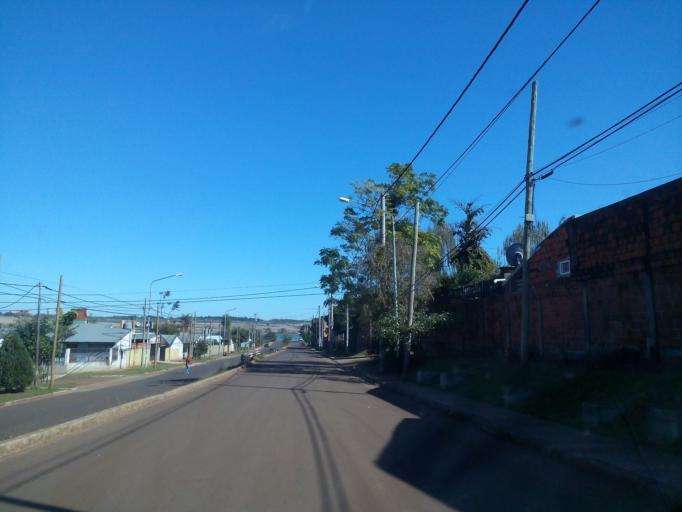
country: AR
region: Misiones
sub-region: Departamento de Capital
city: Posadas
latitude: -27.3861
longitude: -55.9462
